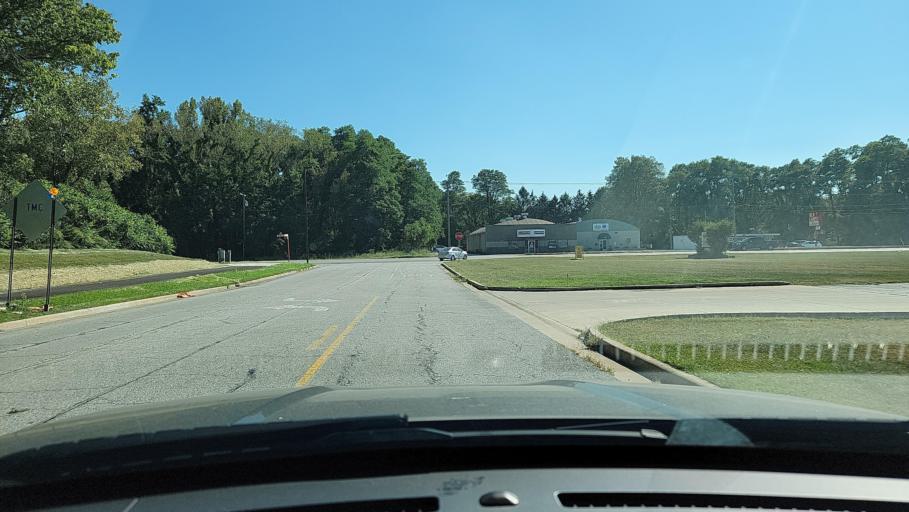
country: US
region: Indiana
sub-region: Porter County
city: Portage
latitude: 41.5995
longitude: -87.1641
